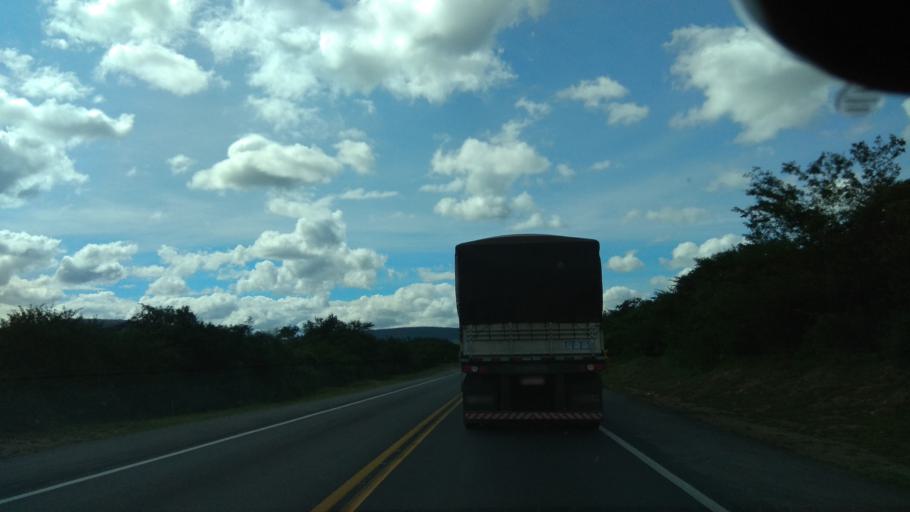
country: BR
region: Bahia
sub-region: Santa Ines
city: Santa Ines
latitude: -13.2888
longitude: -40.0221
